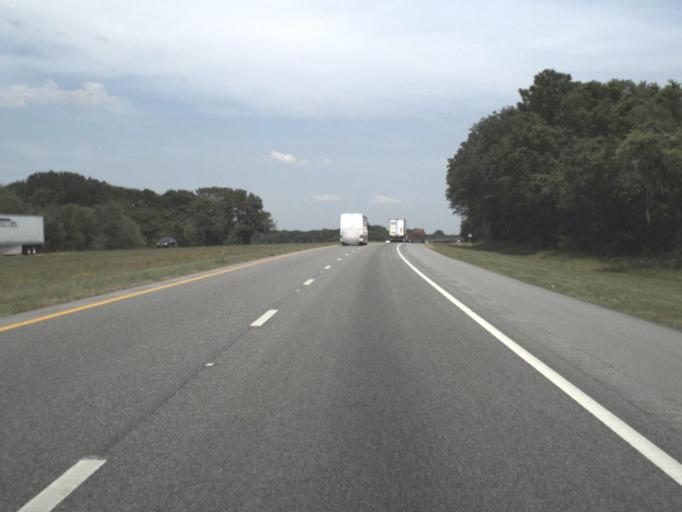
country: US
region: Florida
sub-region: Suwannee County
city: Live Oak
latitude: 30.3488
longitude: -83.0759
